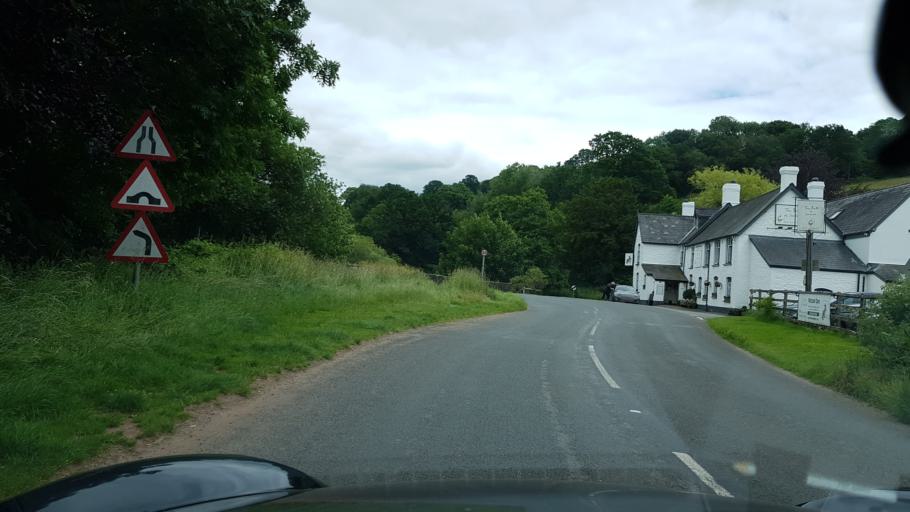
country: GB
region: England
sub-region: Herefordshire
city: Llanrothal
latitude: 51.8779
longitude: -2.7895
